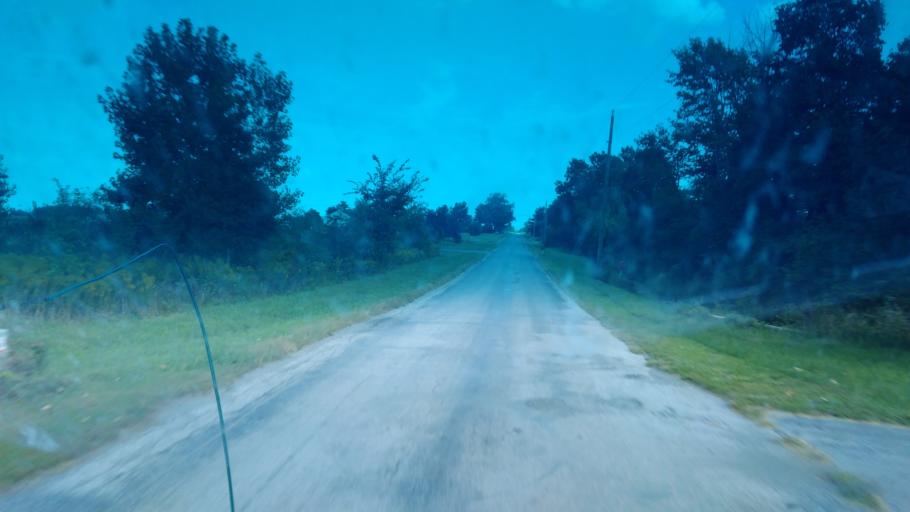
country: US
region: Ohio
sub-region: Hardin County
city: Forest
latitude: 40.9055
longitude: -83.5346
